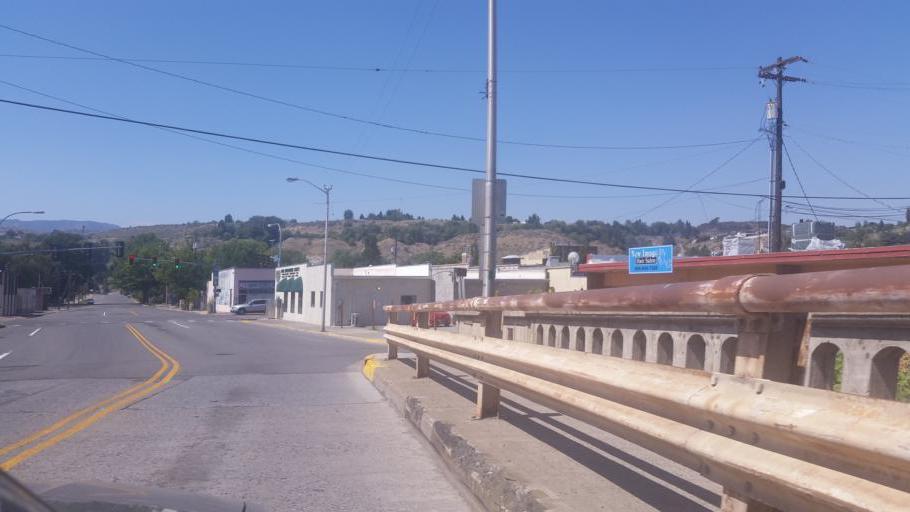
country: US
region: Washington
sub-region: Okanogan County
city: Omak
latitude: 48.4108
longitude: -119.5273
